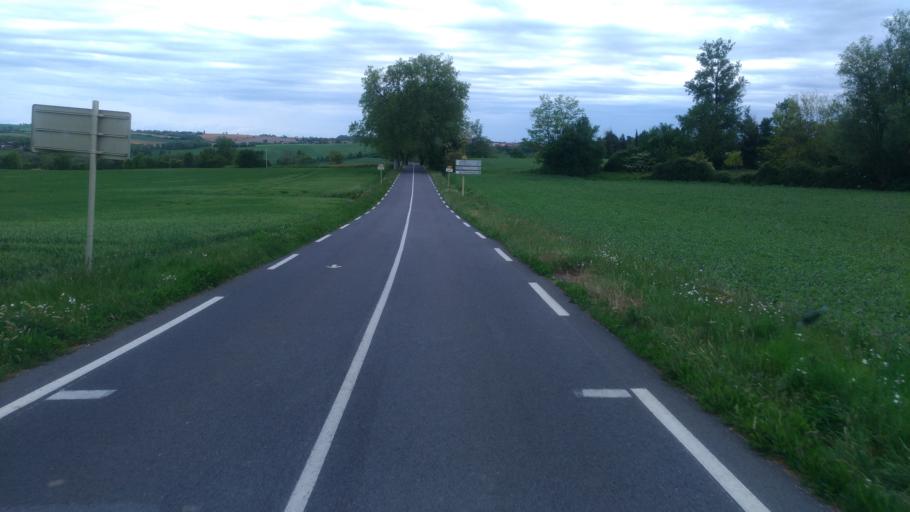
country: FR
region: Midi-Pyrenees
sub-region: Departement de la Haute-Garonne
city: Avignonet-Lauragais
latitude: 43.4371
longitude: 1.7802
